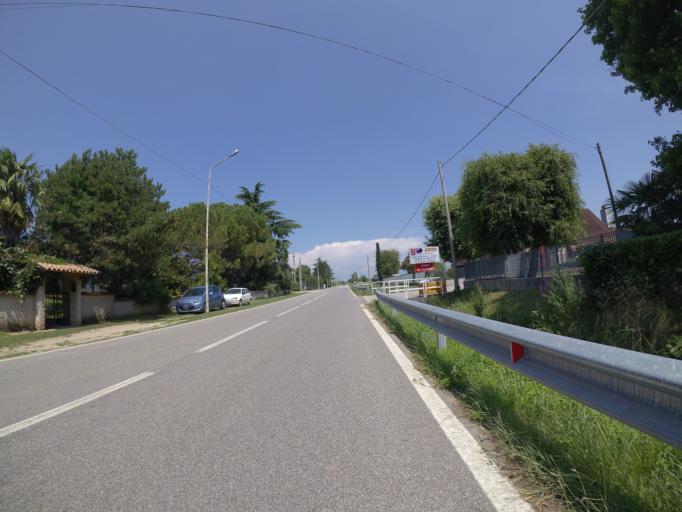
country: IT
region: Friuli Venezia Giulia
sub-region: Provincia di Udine
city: Bertiolo
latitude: 45.9517
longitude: 13.0548
